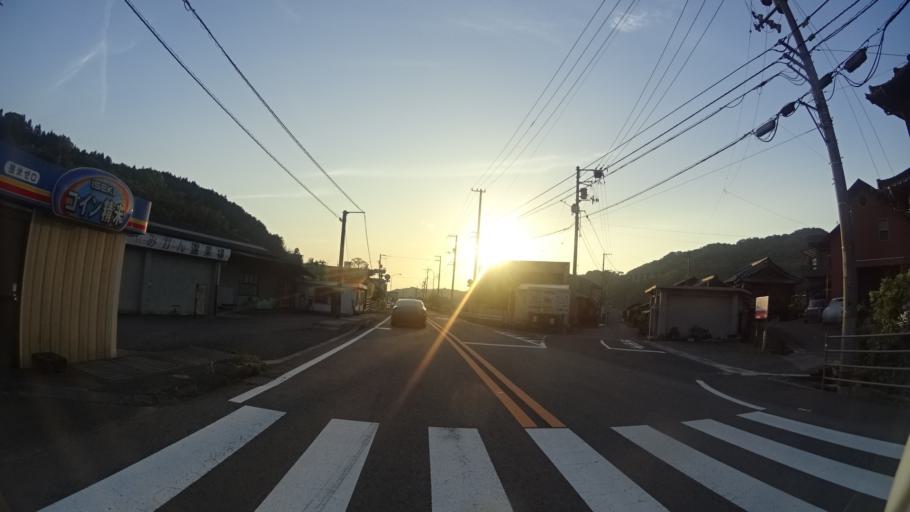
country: JP
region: Ehime
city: Kawanoecho
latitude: 33.9923
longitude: 133.6151
